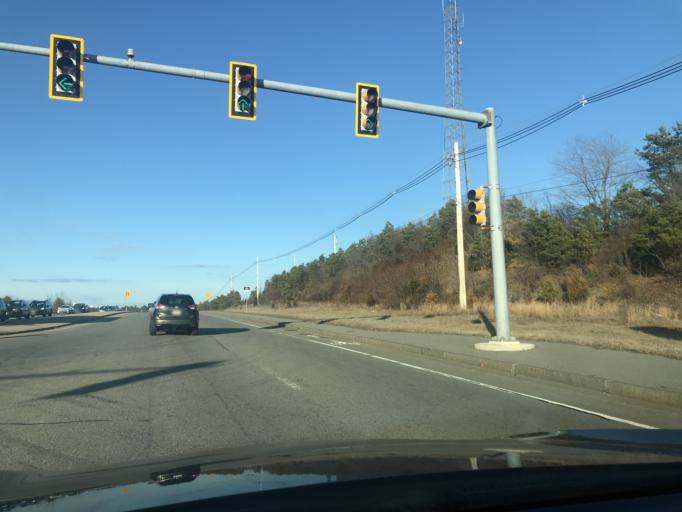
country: US
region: Massachusetts
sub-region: Plymouth County
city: North Plymouth
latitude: 41.9564
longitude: -70.7109
